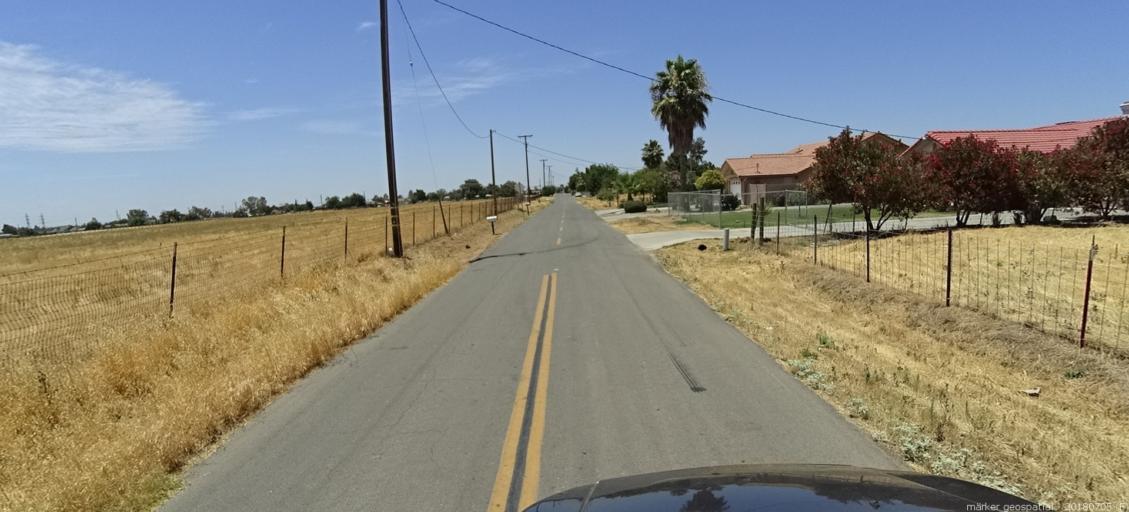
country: US
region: California
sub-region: Madera County
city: Parksdale
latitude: 36.9917
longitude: -120.0246
